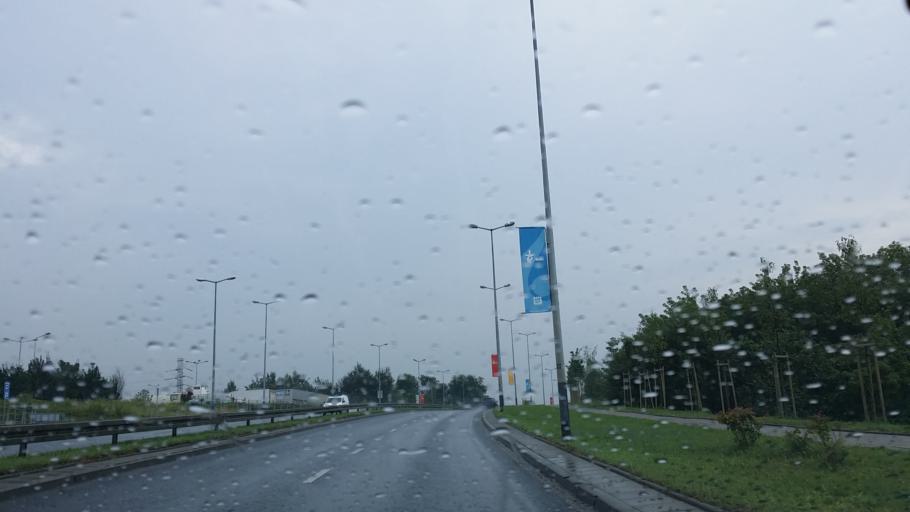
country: PL
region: Lesser Poland Voivodeship
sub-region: Krakow
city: Krakow
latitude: 50.0239
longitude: 19.9456
